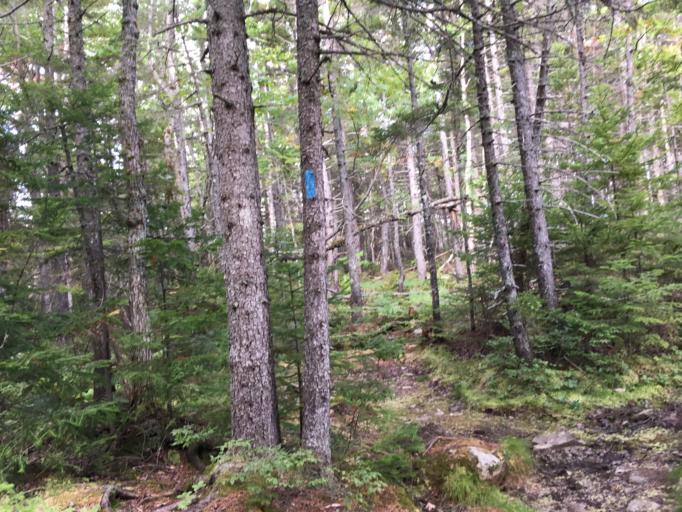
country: US
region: Maine
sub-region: Penobscot County
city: Millinocket
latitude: 45.9190
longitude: -68.8518
